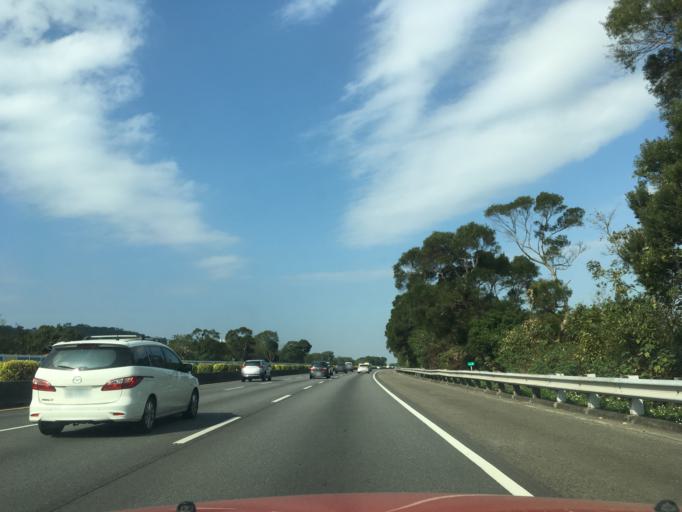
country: TW
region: Taiwan
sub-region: Hsinchu
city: Zhubei
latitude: 24.7581
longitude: 121.0561
